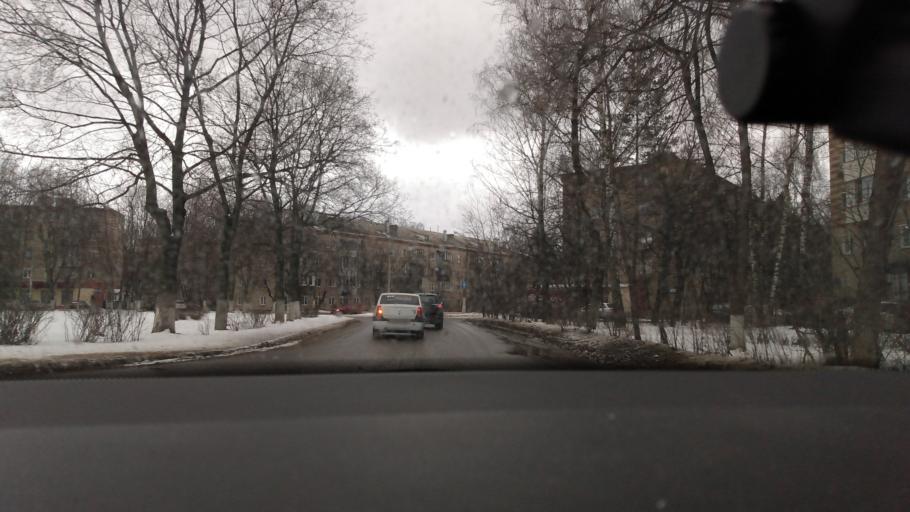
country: RU
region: Moskovskaya
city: Shchelkovo
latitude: 55.9139
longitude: 37.9882
